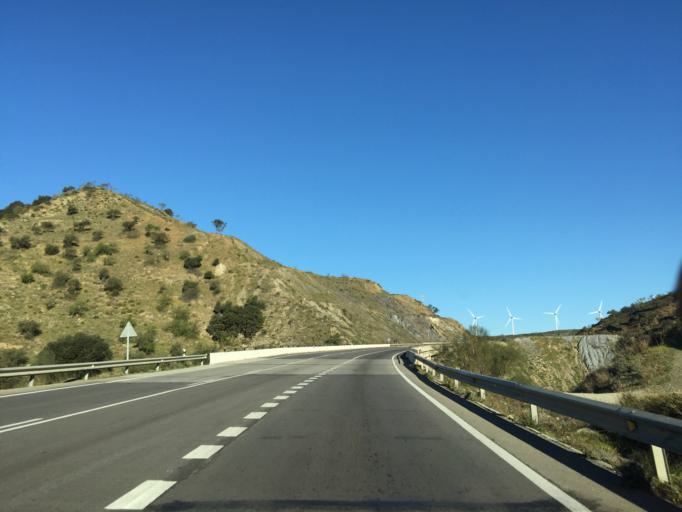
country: ES
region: Andalusia
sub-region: Provincia de Malaga
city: Carratraca
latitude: 36.8492
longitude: -4.8244
